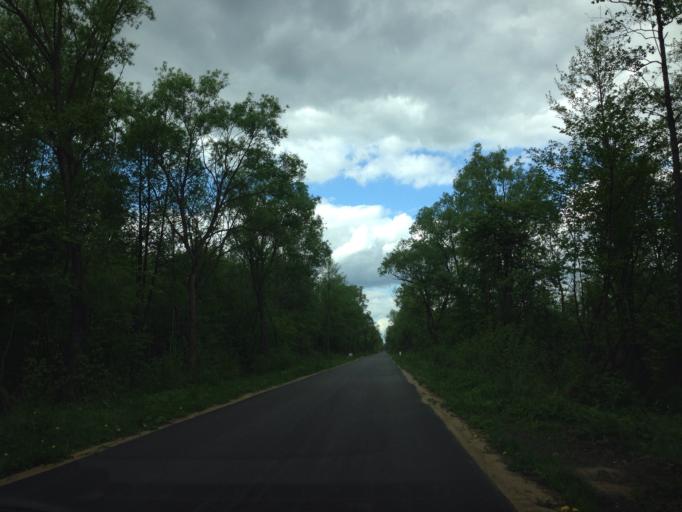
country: PL
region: Podlasie
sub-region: Powiat bialostocki
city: Tykocin
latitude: 53.3006
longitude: 22.6047
